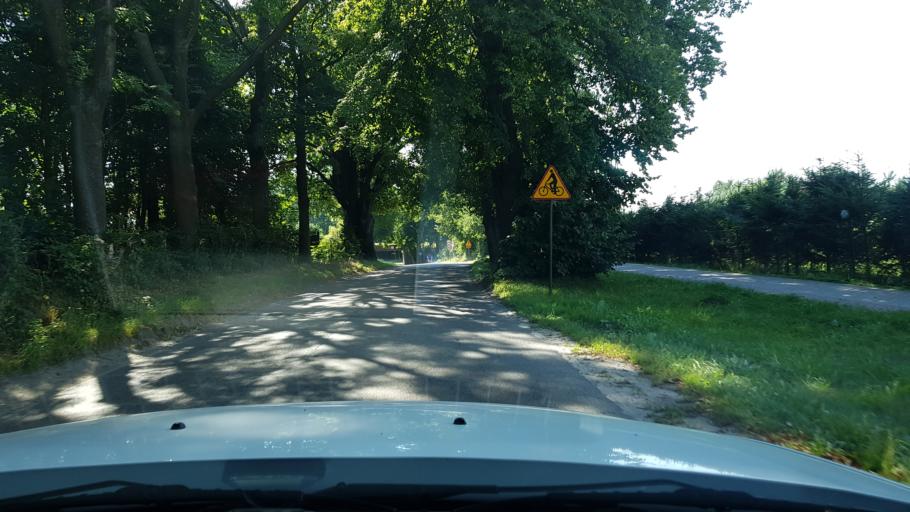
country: PL
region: West Pomeranian Voivodeship
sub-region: Powiat koszalinski
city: Sianow
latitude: 54.2438
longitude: 16.2911
